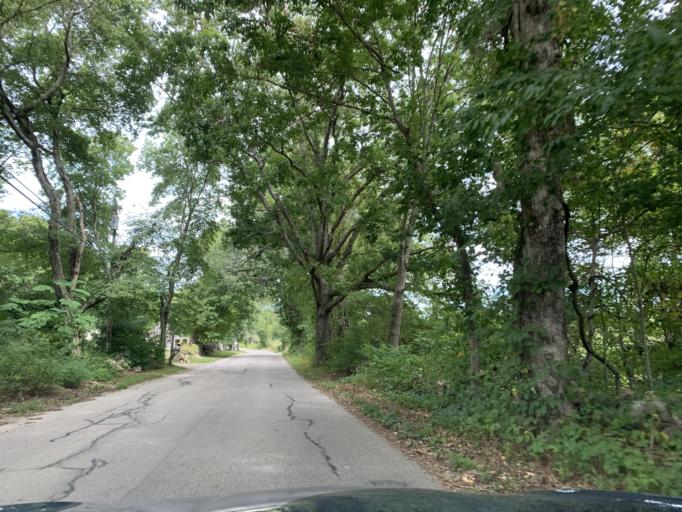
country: US
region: Rhode Island
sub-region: Washington County
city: Exeter
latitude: 41.5591
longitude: -71.6221
